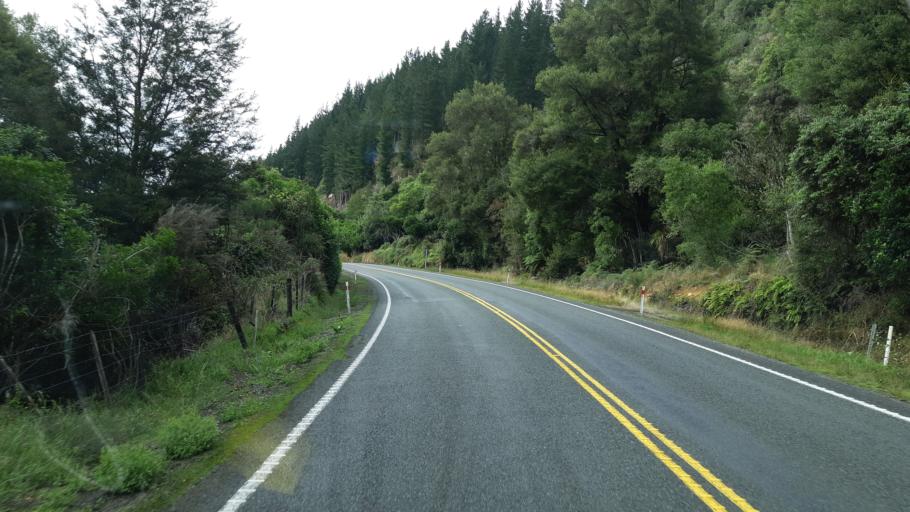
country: NZ
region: West Coast
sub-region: Buller District
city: Westport
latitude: -41.7783
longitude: 172.2473
